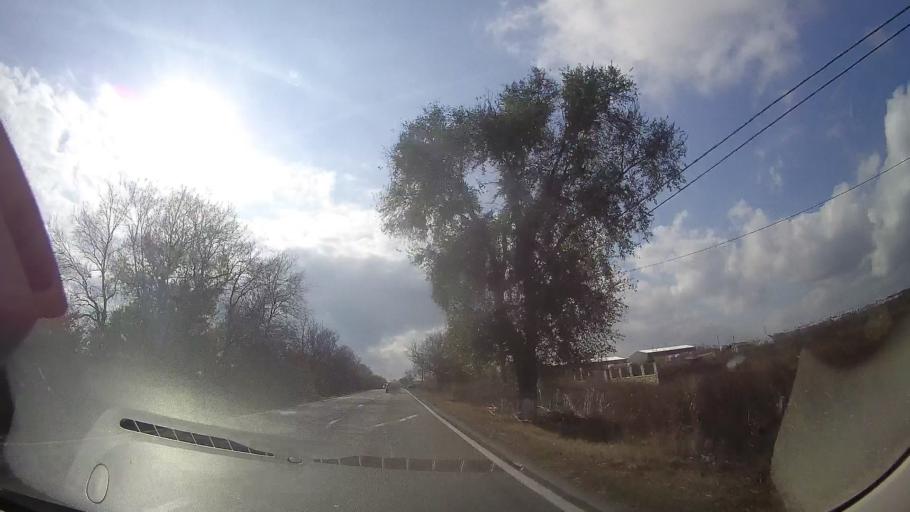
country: RO
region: Constanta
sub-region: Comuna Agigea
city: Agigea
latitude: 44.0837
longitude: 28.6062
